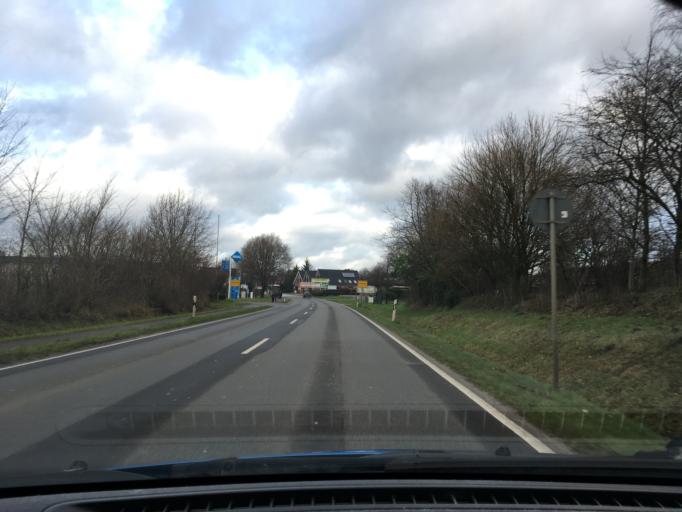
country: DE
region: Schleswig-Holstein
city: Poschendorf
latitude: 54.0386
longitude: 9.4805
